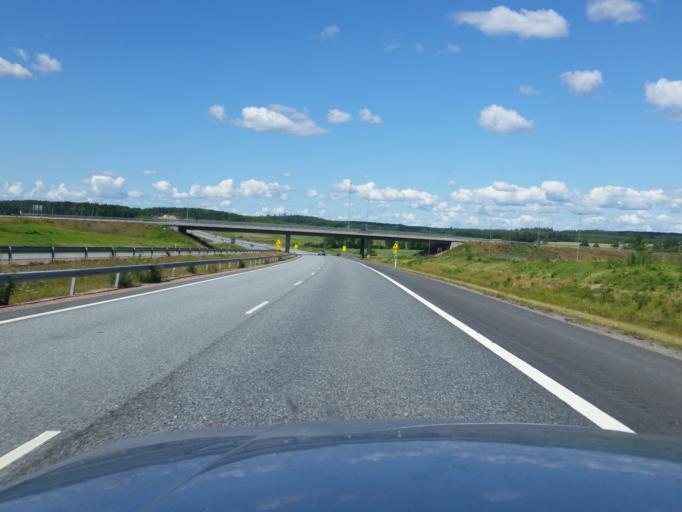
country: FI
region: Varsinais-Suomi
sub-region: Salo
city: Suomusjaervi
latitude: 60.3885
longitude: 23.5888
